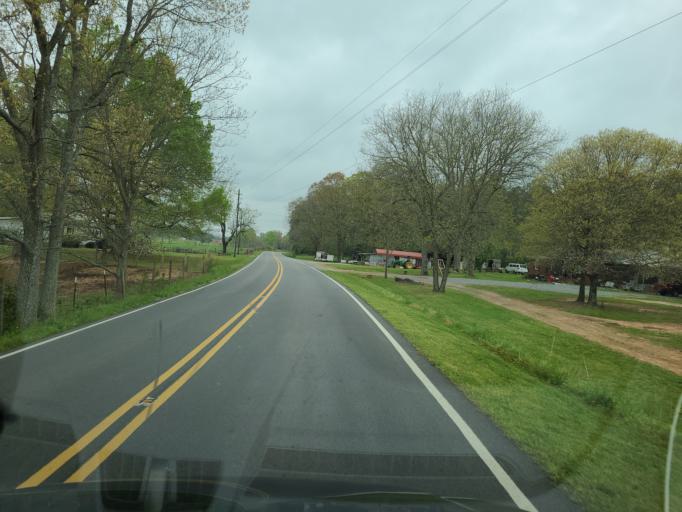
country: US
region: North Carolina
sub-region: Gaston County
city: Cherryville
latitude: 35.4356
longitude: -81.4233
